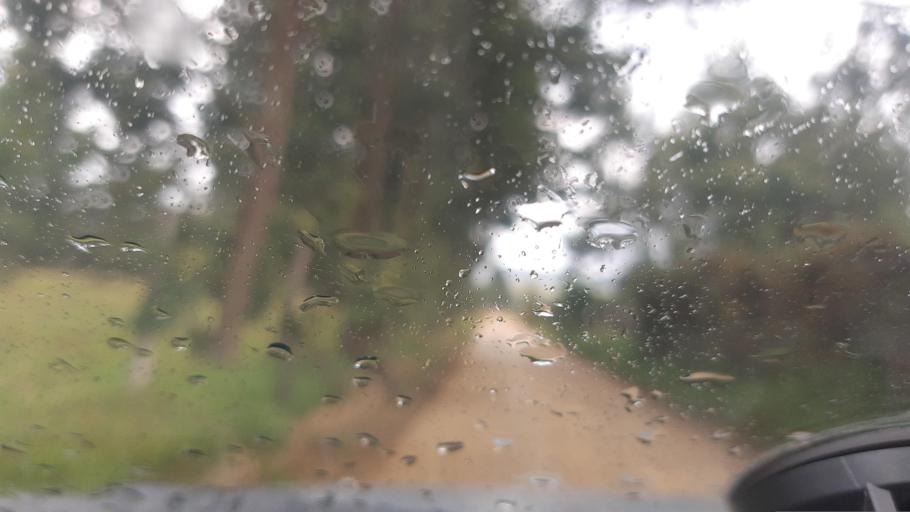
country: CO
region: Cundinamarca
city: Cucunuba
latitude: 5.1939
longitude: -73.7902
